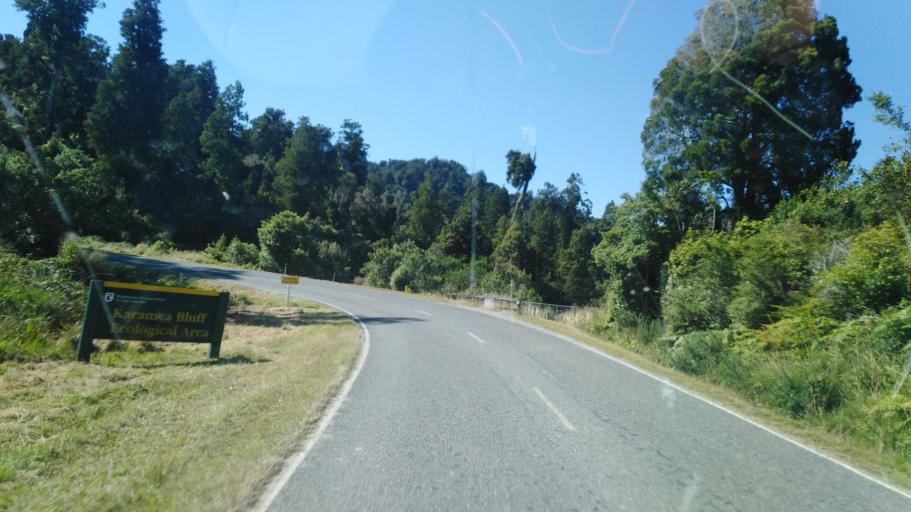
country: NZ
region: West Coast
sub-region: Buller District
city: Westport
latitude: -41.5343
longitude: 171.9918
